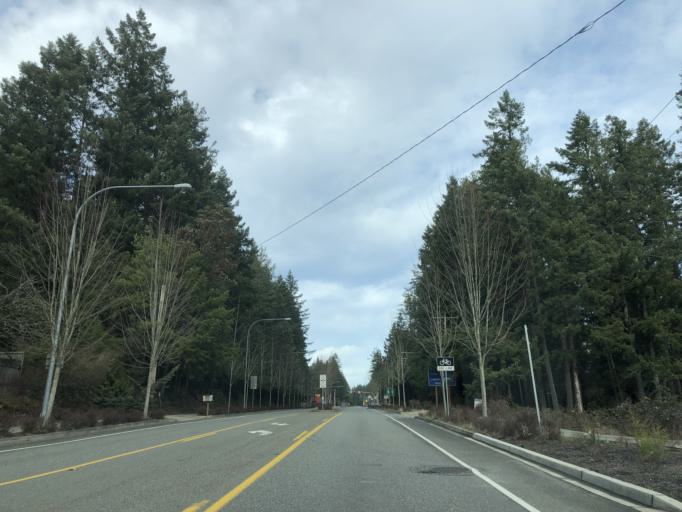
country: US
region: Washington
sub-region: Kitsap County
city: Poulsbo
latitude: 47.7551
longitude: -122.6529
